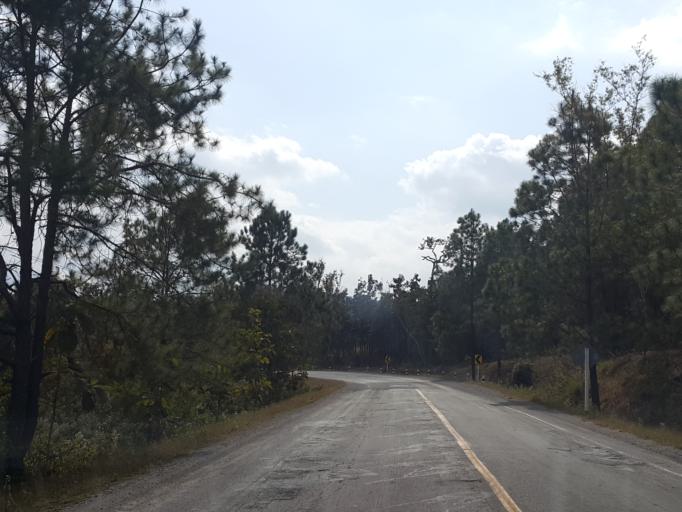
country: TH
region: Chiang Mai
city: Om Koi
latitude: 17.8236
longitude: 98.3592
